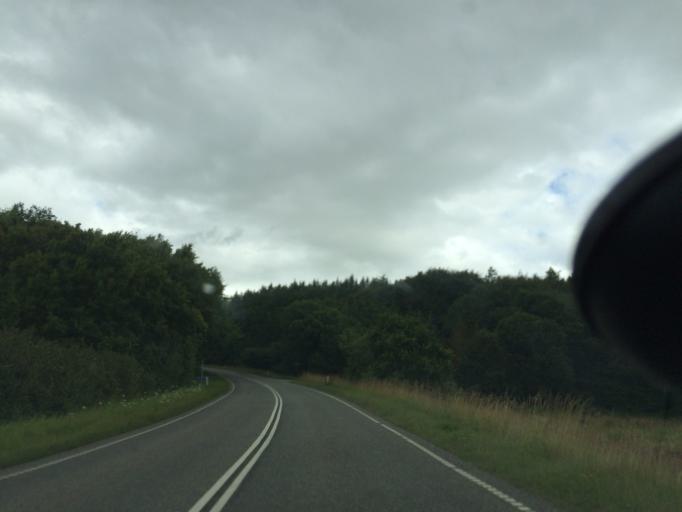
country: DK
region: Central Jutland
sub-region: Skanderborg Kommune
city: Ry
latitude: 56.1654
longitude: 9.8121
